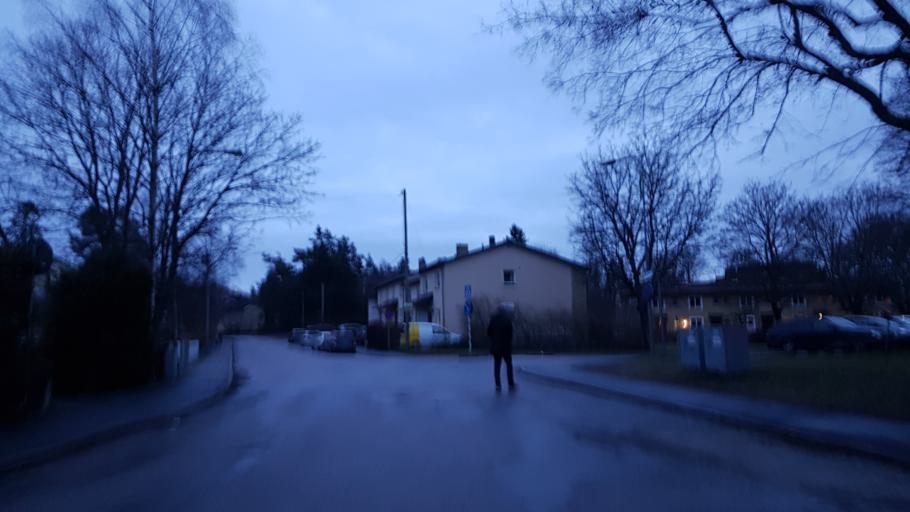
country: SE
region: Stockholm
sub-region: Stockholms Kommun
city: Arsta
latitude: 59.2742
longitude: 18.0537
